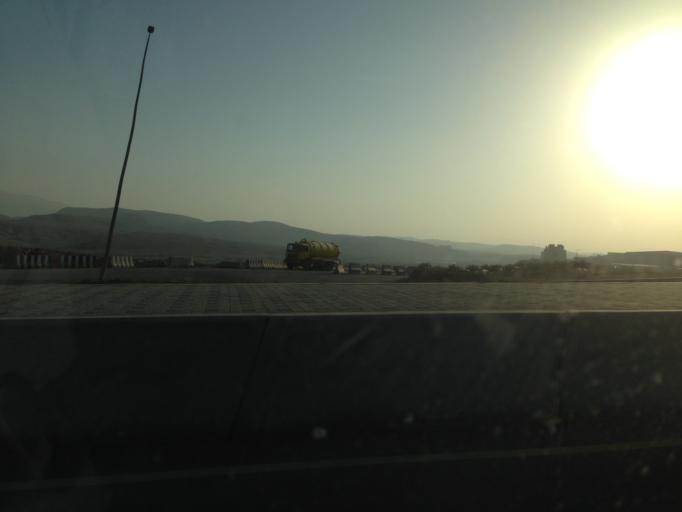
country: OM
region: Muhafazat Masqat
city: Bawshar
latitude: 23.5684
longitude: 58.3355
